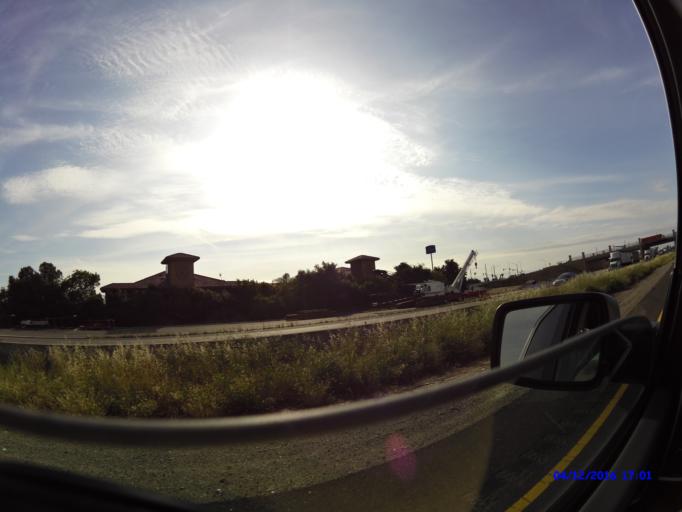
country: US
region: California
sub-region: Stanislaus County
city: Salida
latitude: 37.6976
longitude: -121.0694
